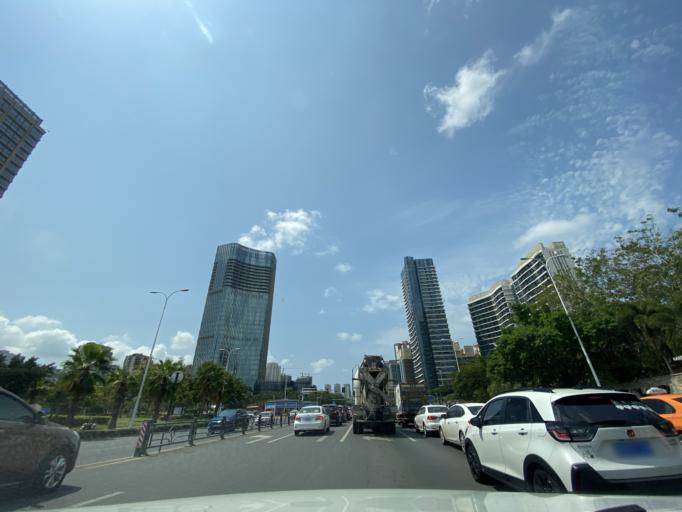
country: CN
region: Hainan
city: Sanya
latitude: 18.2779
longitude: 109.5098
